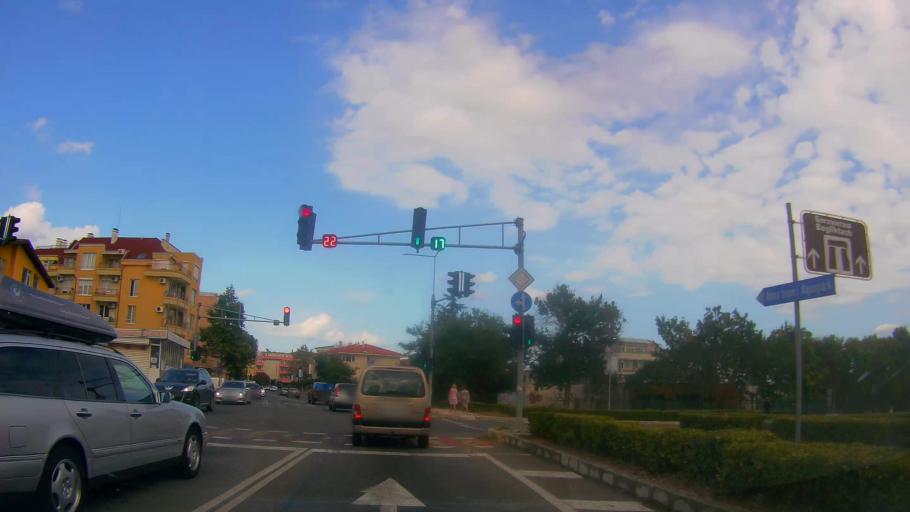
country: BG
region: Burgas
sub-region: Obshtina Primorsko
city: Primorsko
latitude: 42.2657
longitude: 27.7472
